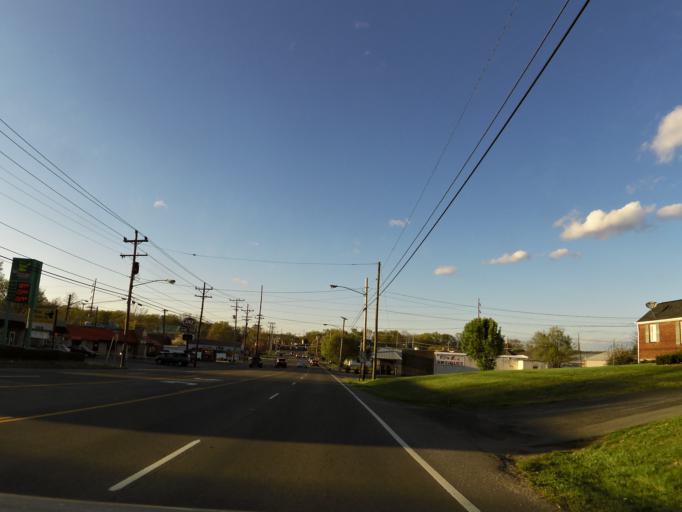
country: US
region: Tennessee
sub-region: Davidson County
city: Goodlettsville
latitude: 36.3195
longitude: -86.7131
